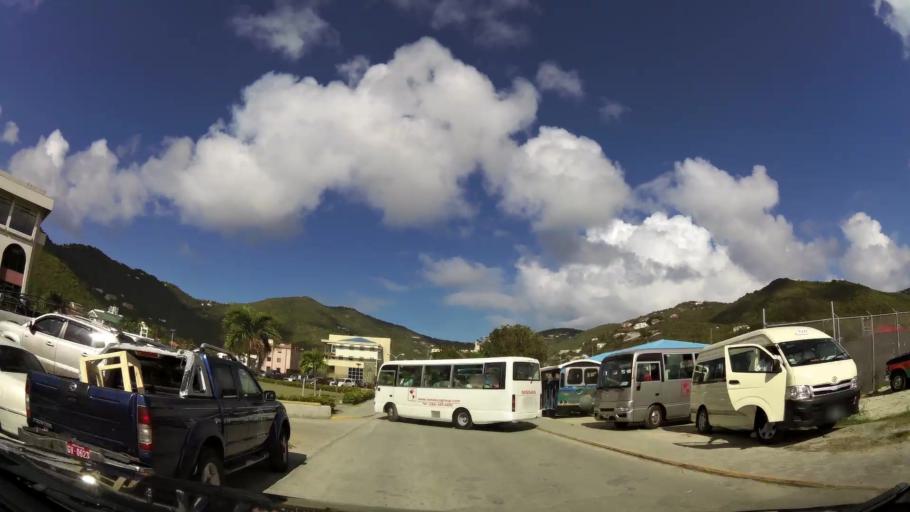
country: VG
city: Road Town
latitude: 18.4220
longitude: -64.6154
